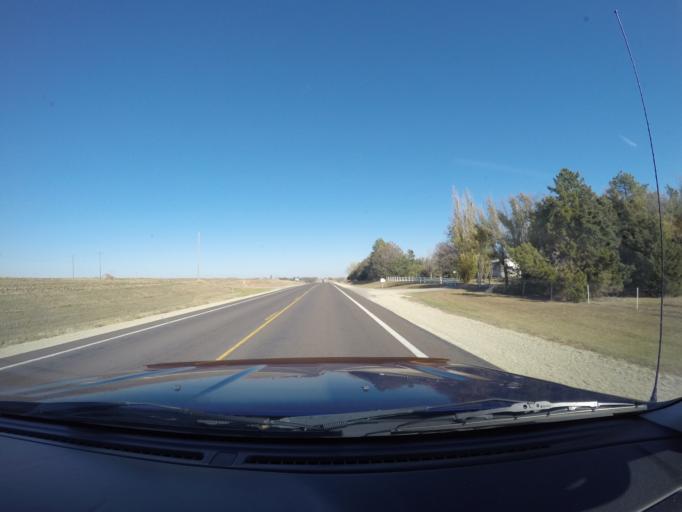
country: US
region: Kansas
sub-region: Marshall County
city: Blue Rapids
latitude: 39.6574
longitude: -96.7505
